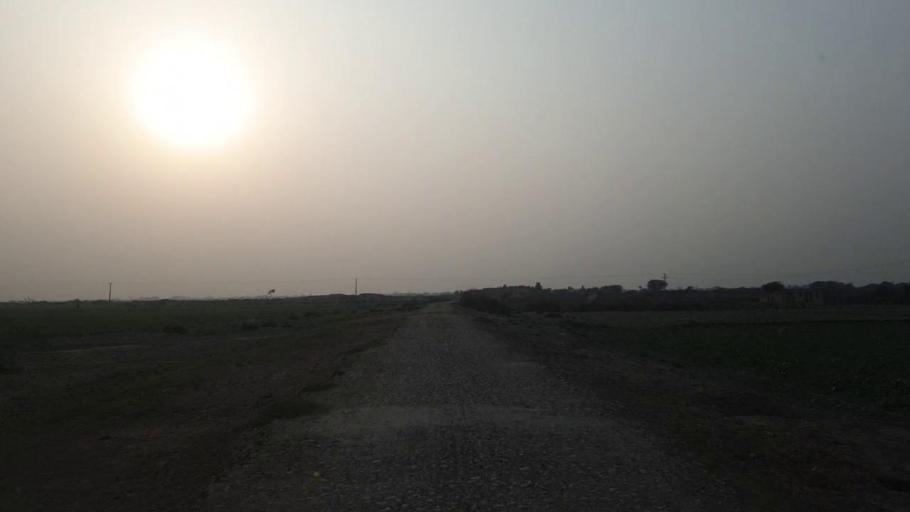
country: PK
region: Sindh
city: Mirpur Batoro
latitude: 24.6636
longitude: 68.3784
